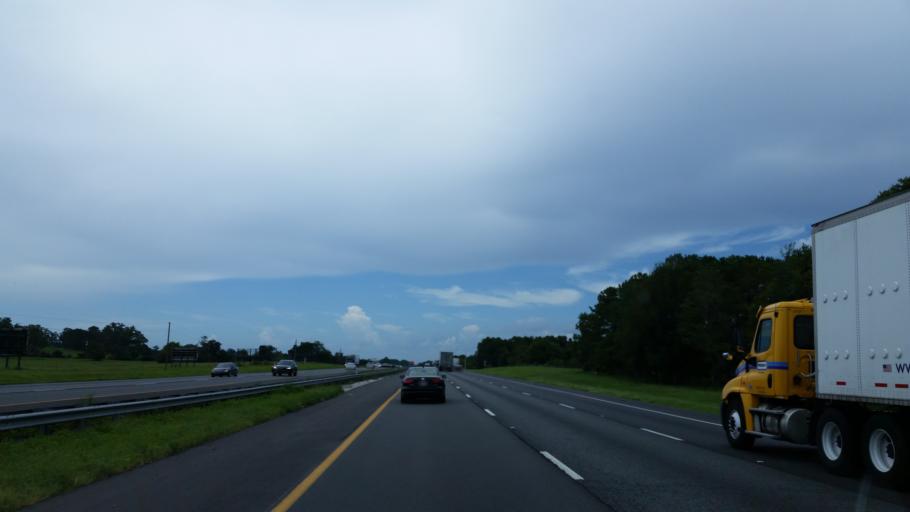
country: US
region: Florida
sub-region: Marion County
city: Citra
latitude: 29.3121
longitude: -82.2088
